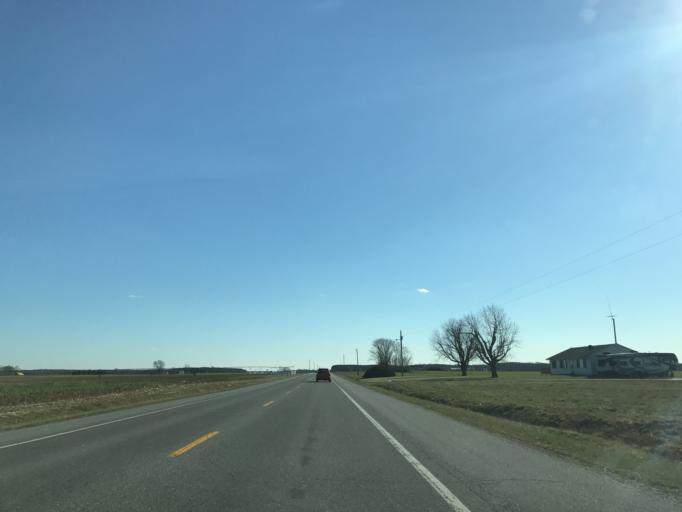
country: US
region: Maryland
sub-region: Caroline County
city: Greensboro
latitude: 39.1268
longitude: -75.8666
